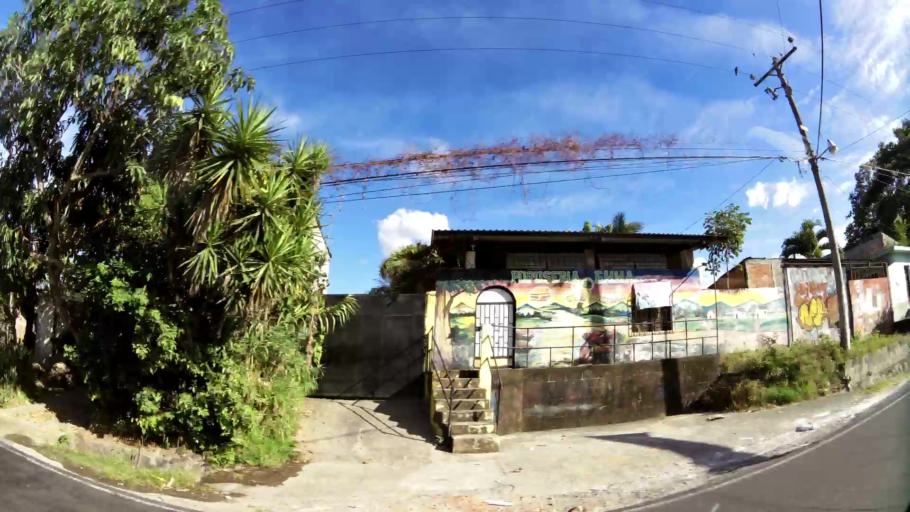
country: SV
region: Cuscatlan
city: Tecoluca
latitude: 13.7663
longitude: -89.0464
